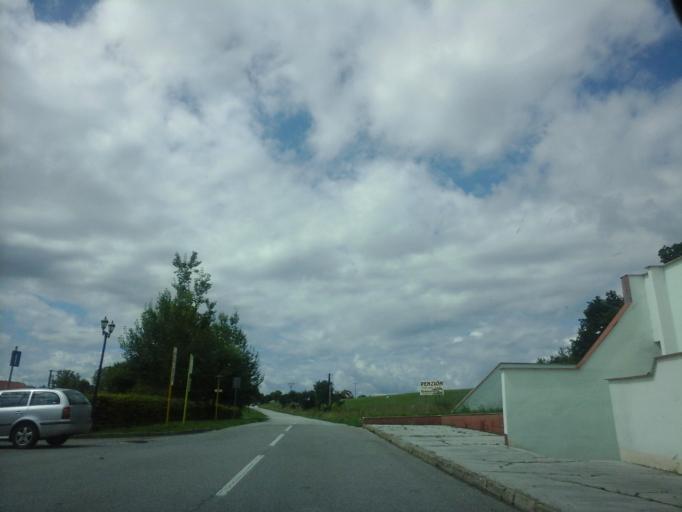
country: HU
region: Borsod-Abauj-Zemplen
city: Putnok
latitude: 48.4776
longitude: 20.4693
